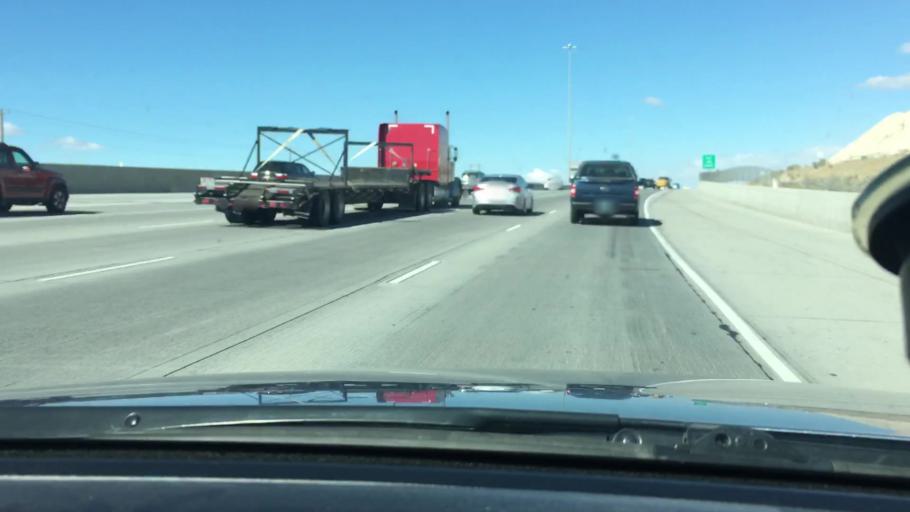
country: US
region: Utah
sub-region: Salt Lake County
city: Bluffdale
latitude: 40.4514
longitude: -111.9129
